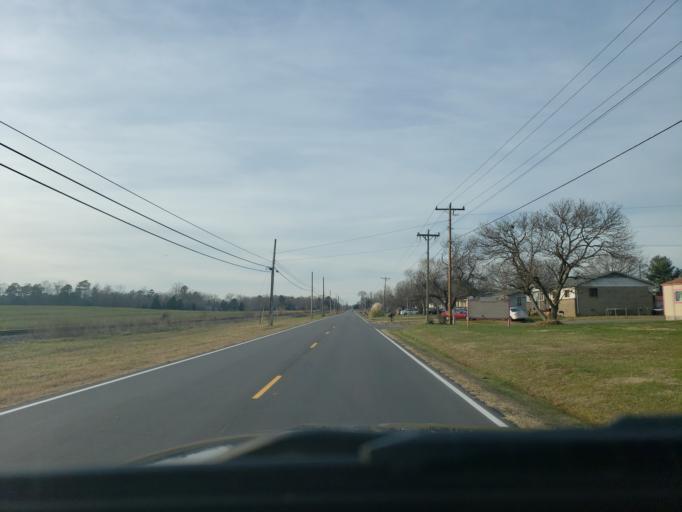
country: US
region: North Carolina
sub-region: Cleveland County
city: Boiling Springs
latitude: 35.3130
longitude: -81.7386
